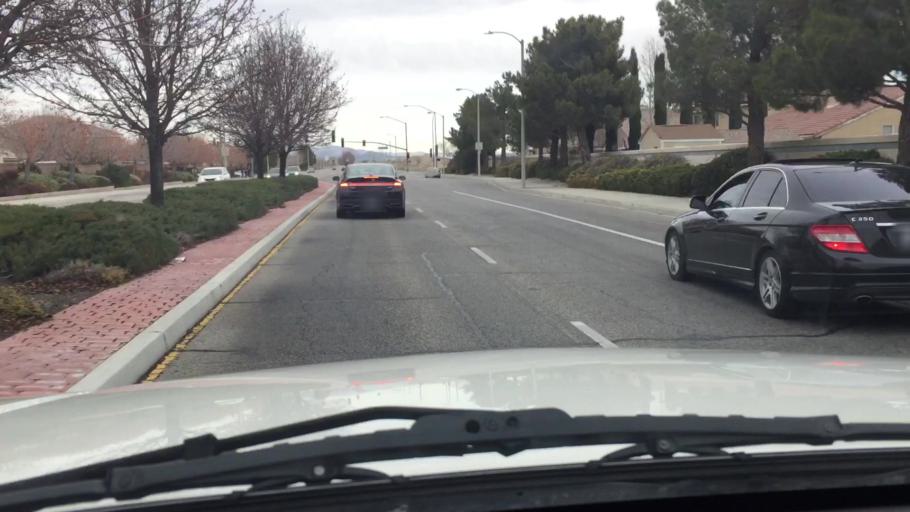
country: US
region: California
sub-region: Los Angeles County
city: Lancaster
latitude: 34.6951
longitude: -118.1838
